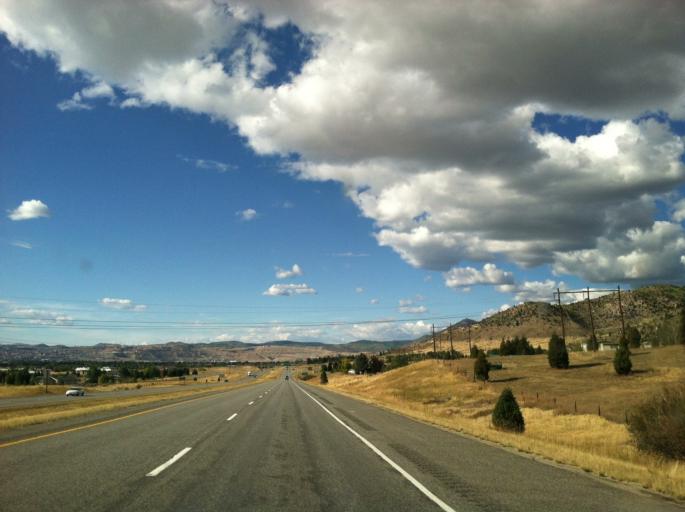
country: US
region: Montana
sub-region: Silver Bow County
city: Butte
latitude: 45.9516
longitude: -112.4672
